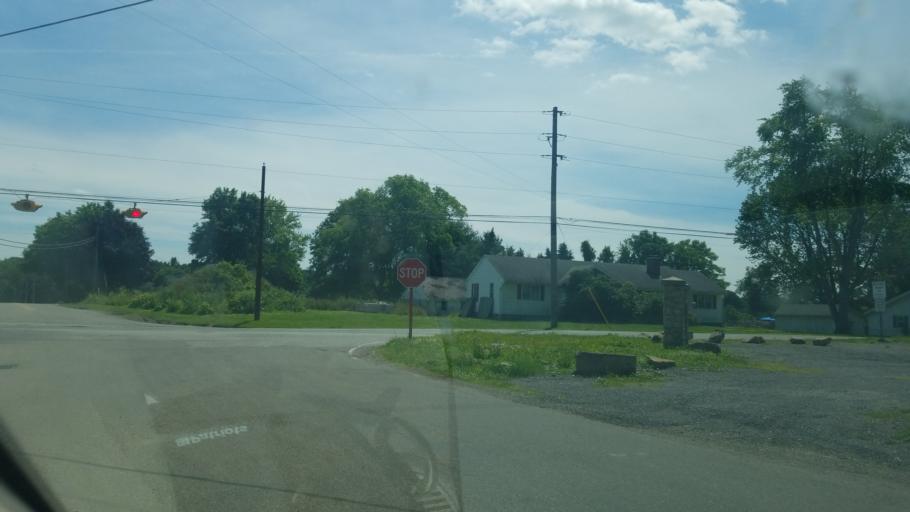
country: US
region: Ohio
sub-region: Stark County
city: Massillon
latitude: 40.8069
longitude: -81.5432
